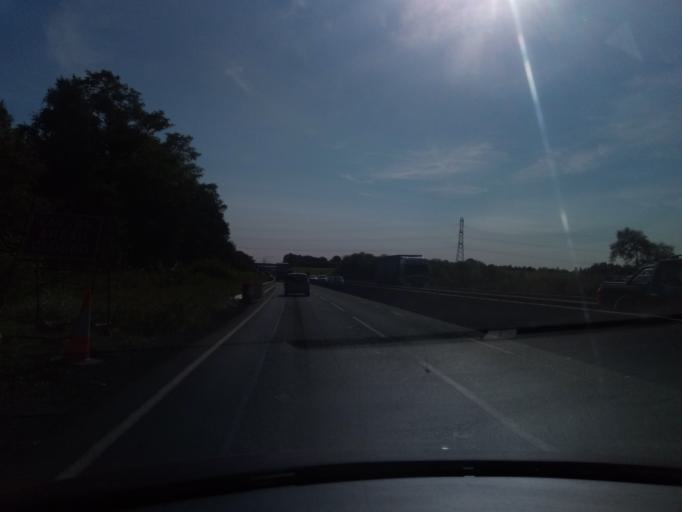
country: GB
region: England
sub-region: Stockton-on-Tees
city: Billingham
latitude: 54.6000
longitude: -1.3082
